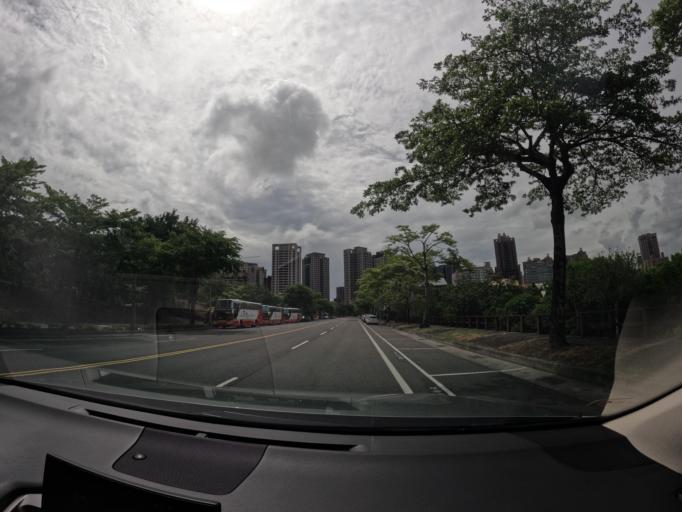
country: TW
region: Kaohsiung
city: Kaohsiung
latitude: 22.6473
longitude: 120.2875
